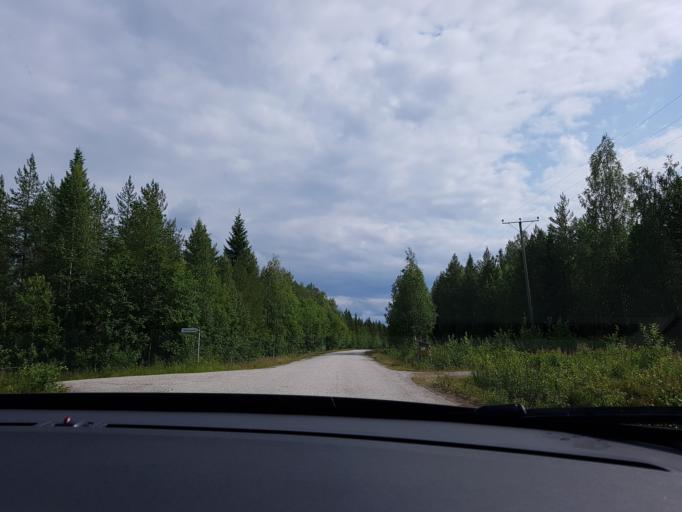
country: FI
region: Kainuu
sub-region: Kehys-Kainuu
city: Kuhmo
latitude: 64.4194
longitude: 29.7611
